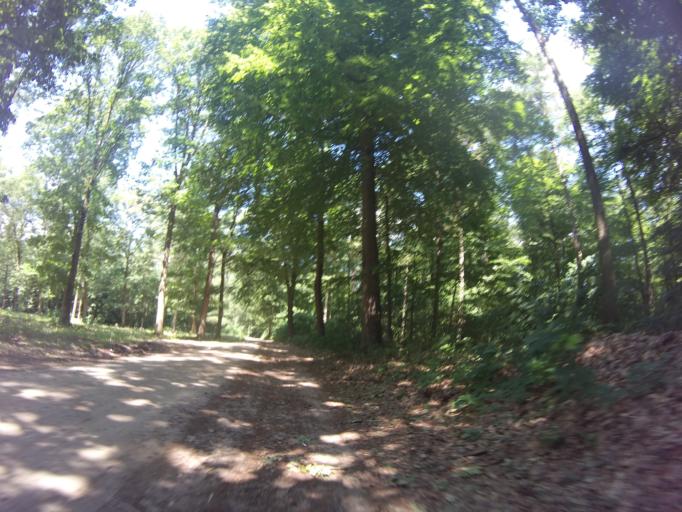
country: NL
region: Drenthe
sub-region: Gemeente Emmen
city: Emmen
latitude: 52.8022
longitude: 6.9109
